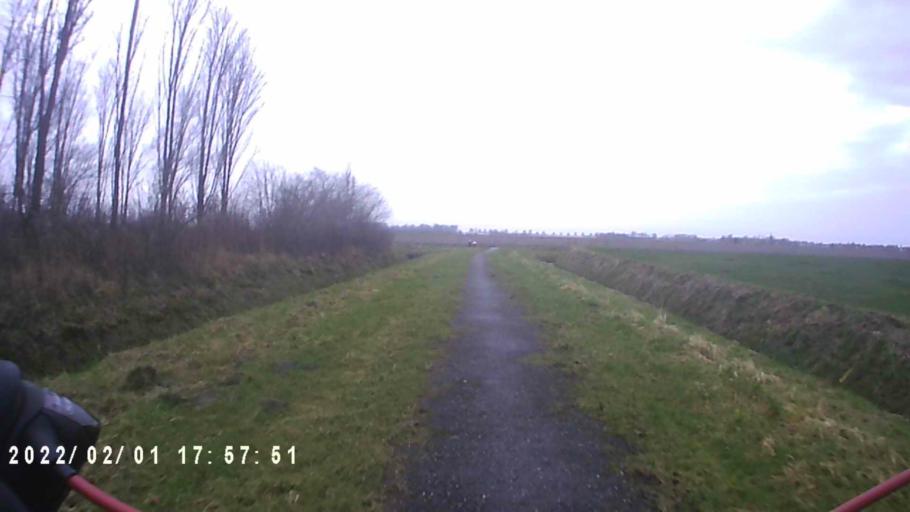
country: NL
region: Groningen
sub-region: Gemeente Zuidhorn
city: Oldehove
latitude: 53.3467
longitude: 6.3918
